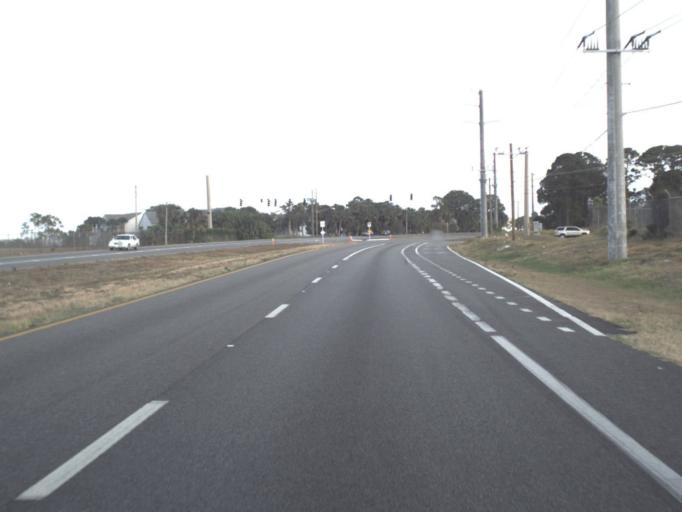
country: US
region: Florida
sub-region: Brevard County
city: Port Saint John
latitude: 28.4919
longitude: -80.7767
